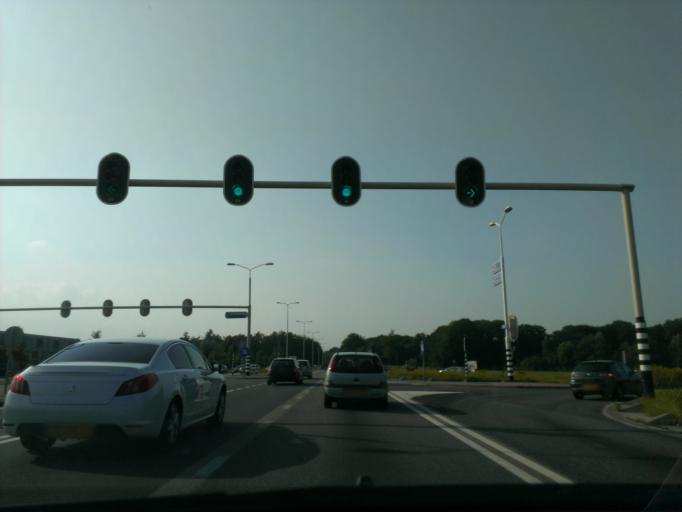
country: NL
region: Gelderland
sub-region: Gemeente Apeldoorn
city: Apeldoorn
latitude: 52.2017
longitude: 6.0363
